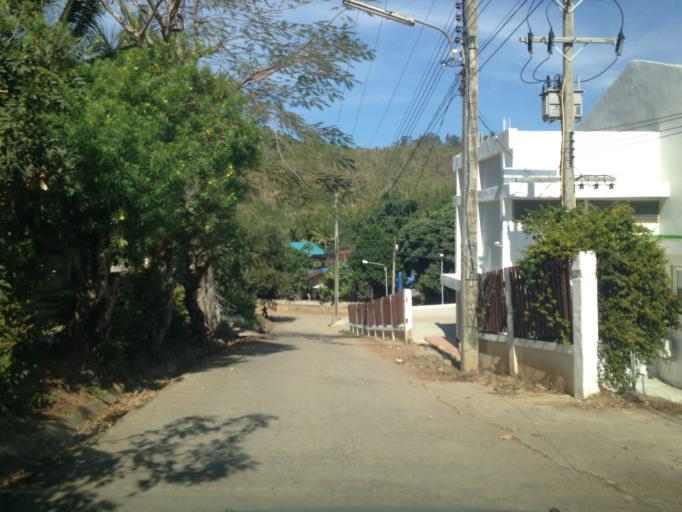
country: TH
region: Mae Hong Son
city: Ban Huai I Huak
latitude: 18.0889
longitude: 98.2019
